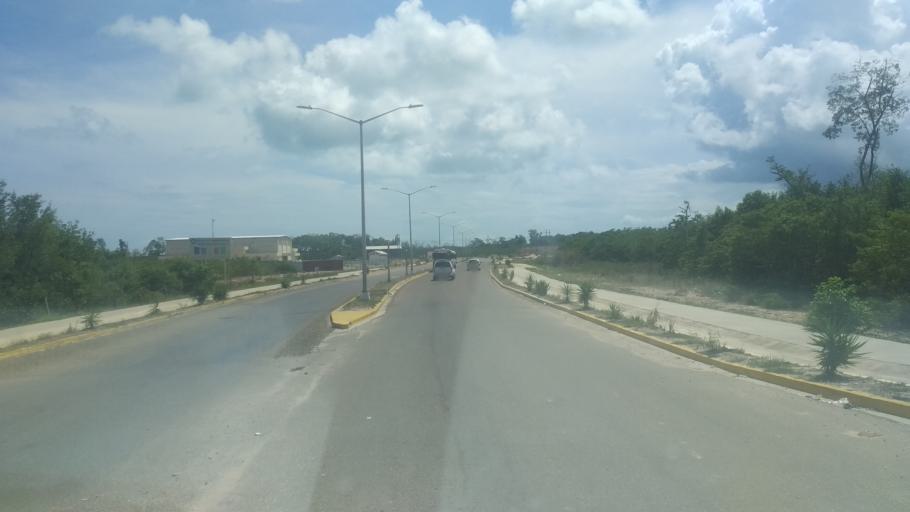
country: BZ
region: Belize
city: Belize City
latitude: 17.5071
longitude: -88.2216
